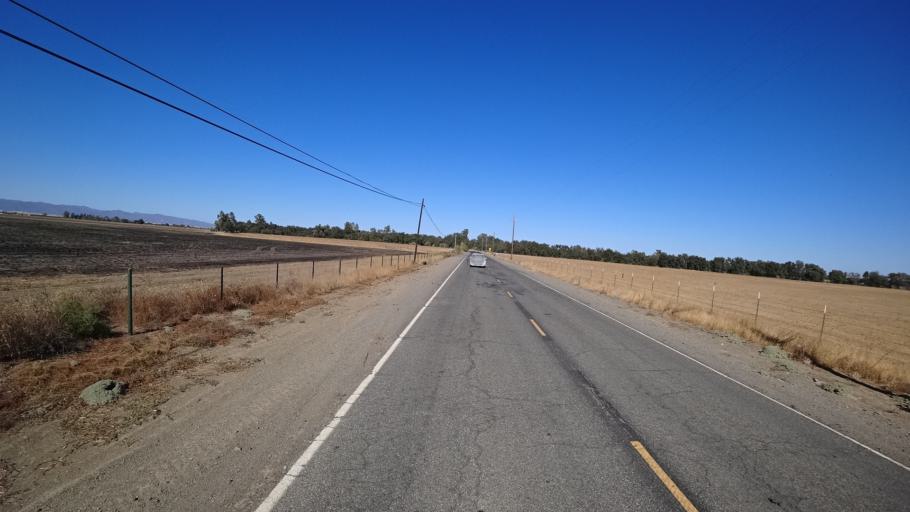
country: US
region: California
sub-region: Solano County
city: Dixon
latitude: 38.5426
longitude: -121.8536
